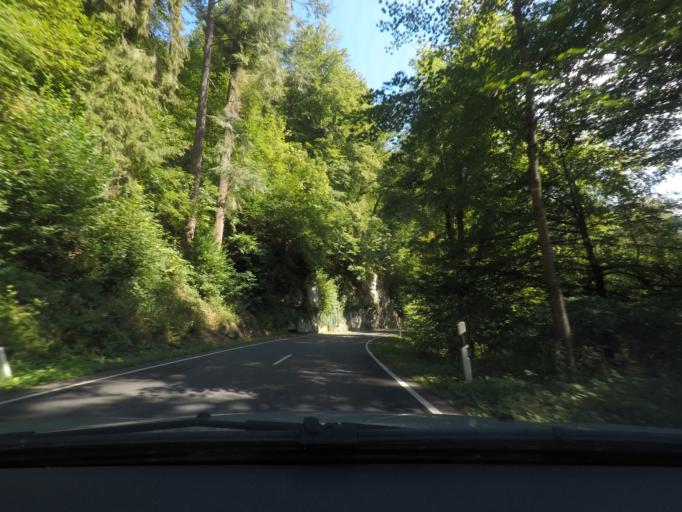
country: LU
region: Grevenmacher
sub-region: Canton d'Echternach
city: Waldbillig
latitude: 49.7730
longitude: 6.2844
